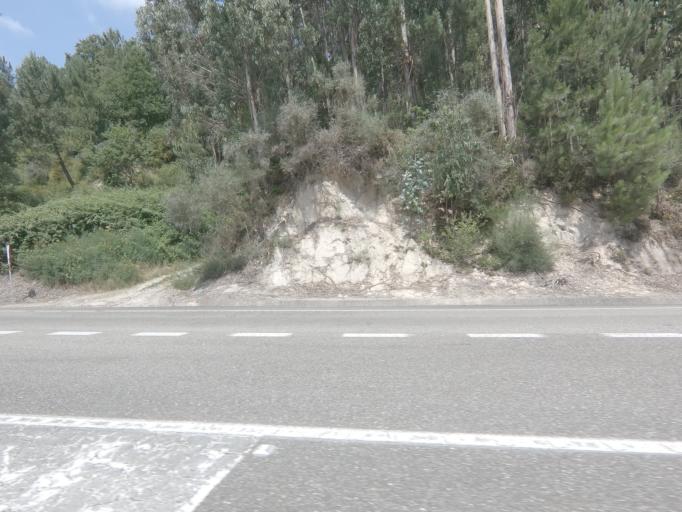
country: ES
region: Galicia
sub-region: Provincia de Pontevedra
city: Tomino
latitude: 42.0477
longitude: -8.7321
